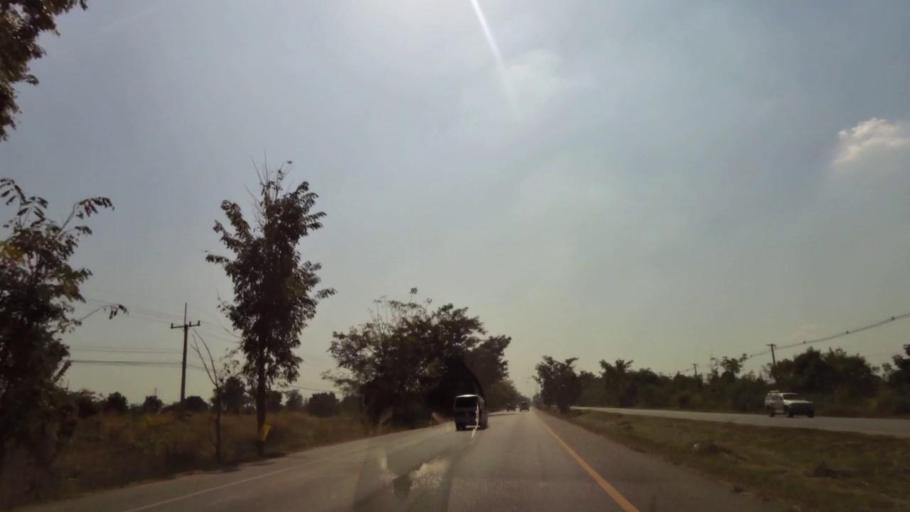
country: TH
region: Phichit
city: Wachira Barami
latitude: 16.3858
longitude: 100.1374
